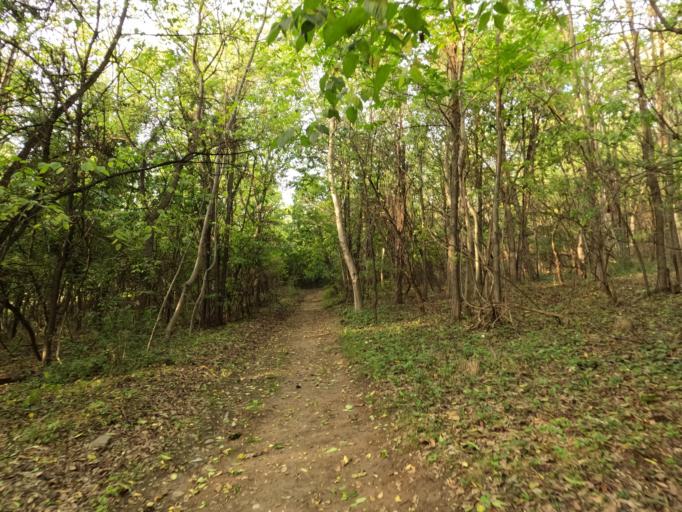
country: HU
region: Tolna
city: Szekszard
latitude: 46.3402
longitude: 18.6723
